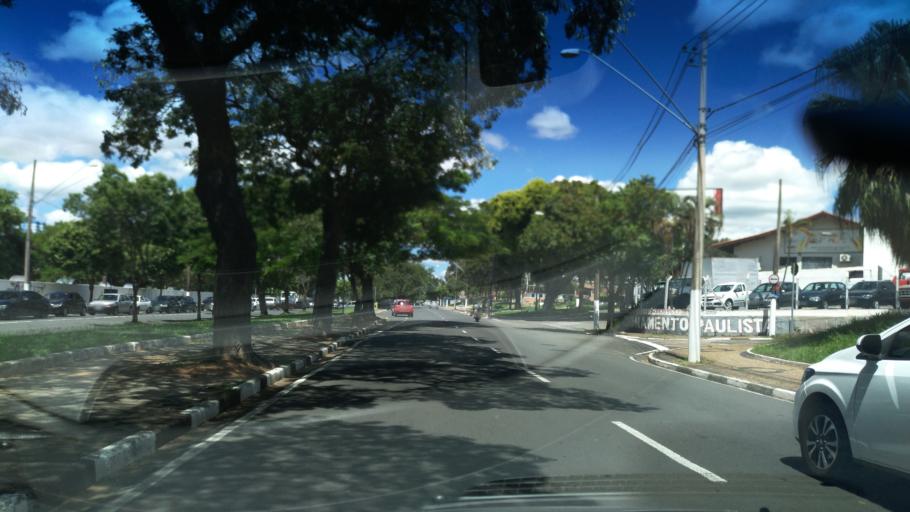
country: BR
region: Sao Paulo
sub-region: Valinhos
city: Valinhos
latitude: -22.9769
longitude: -46.9898
